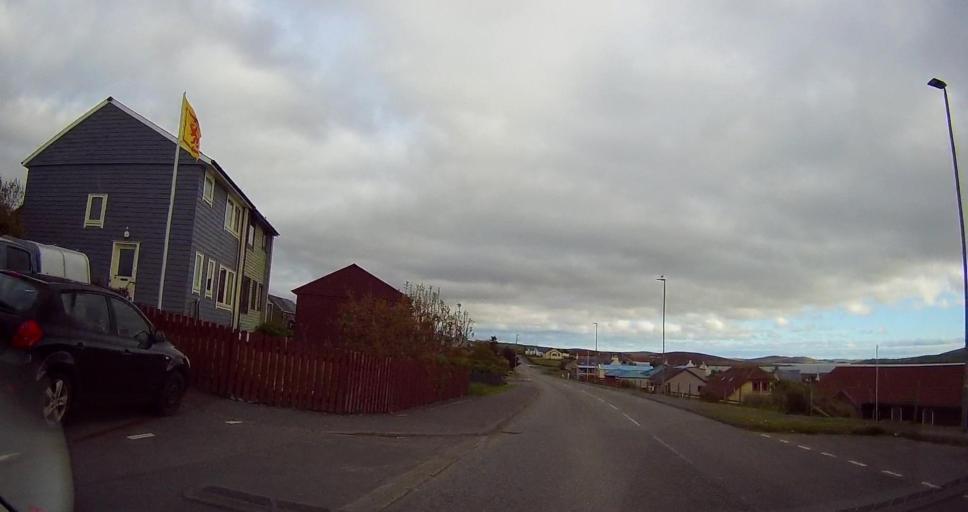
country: GB
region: Scotland
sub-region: Shetland Islands
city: Lerwick
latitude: 60.3913
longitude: -1.3491
